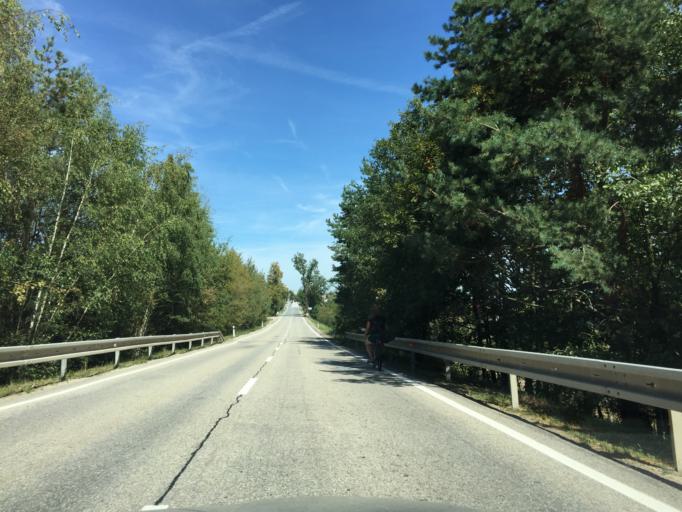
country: CZ
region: Jihocesky
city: Sevetin
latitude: 49.0945
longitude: 14.5601
